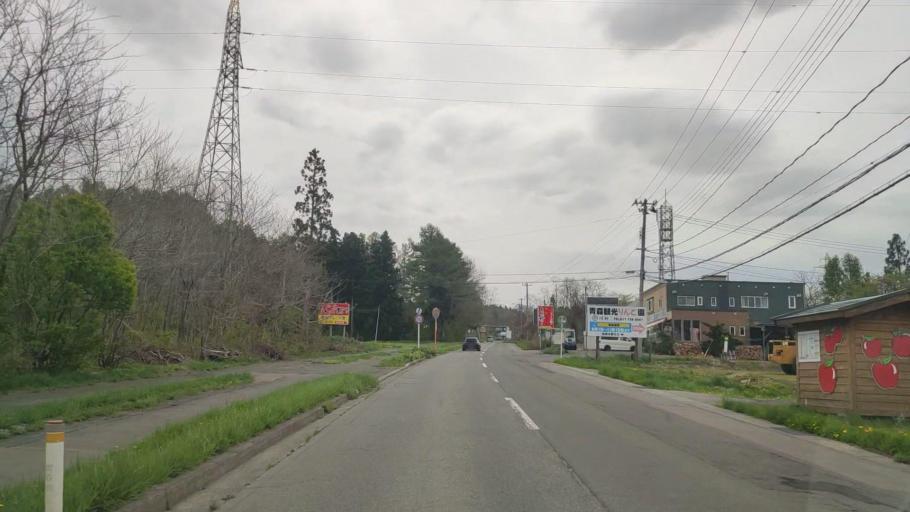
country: JP
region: Aomori
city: Aomori Shi
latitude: 40.7690
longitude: 140.7998
